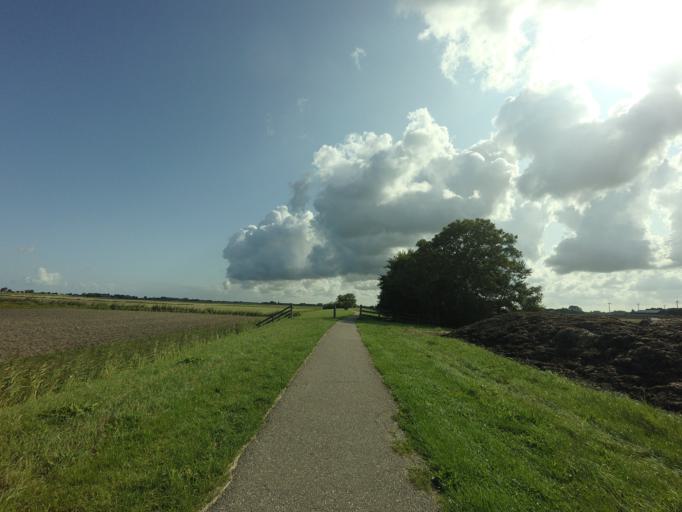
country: NL
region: Friesland
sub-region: Gemeente Franekeradeel
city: Tzummarum
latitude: 53.2630
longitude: 5.5549
